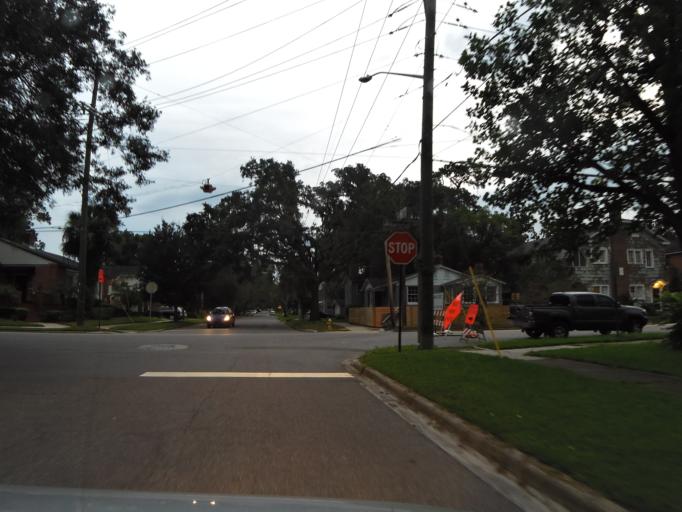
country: US
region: Florida
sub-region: Duval County
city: Jacksonville
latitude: 30.2976
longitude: -81.7077
